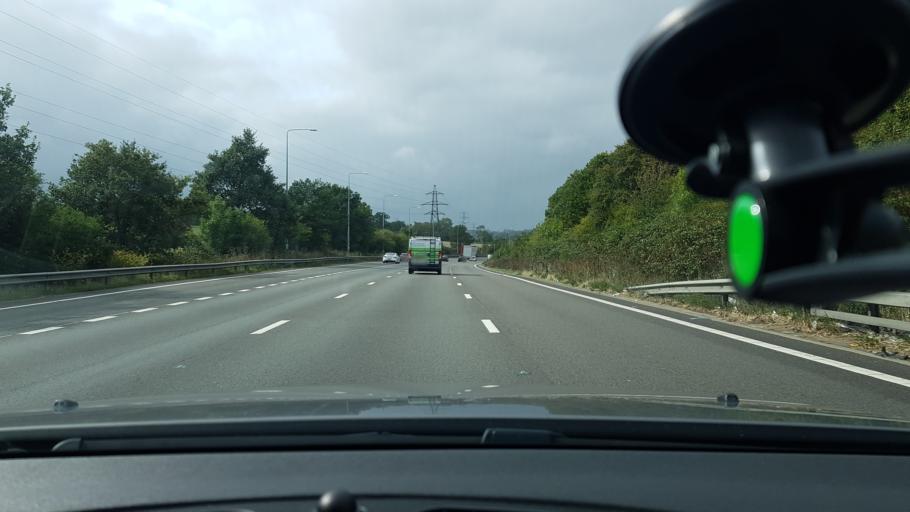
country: GB
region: England
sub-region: Greater London
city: High Barnet
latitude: 51.6848
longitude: -0.2082
